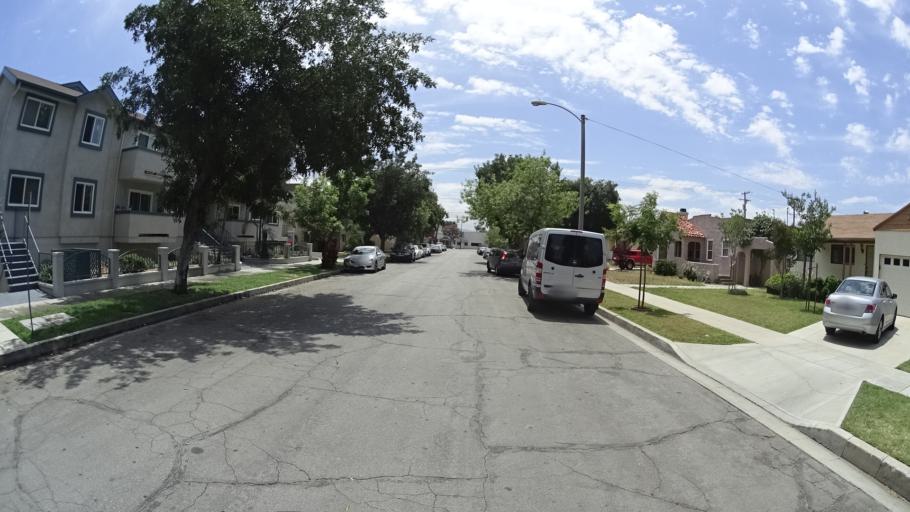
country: US
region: California
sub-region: Los Angeles County
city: Burbank
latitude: 34.1694
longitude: -118.3094
